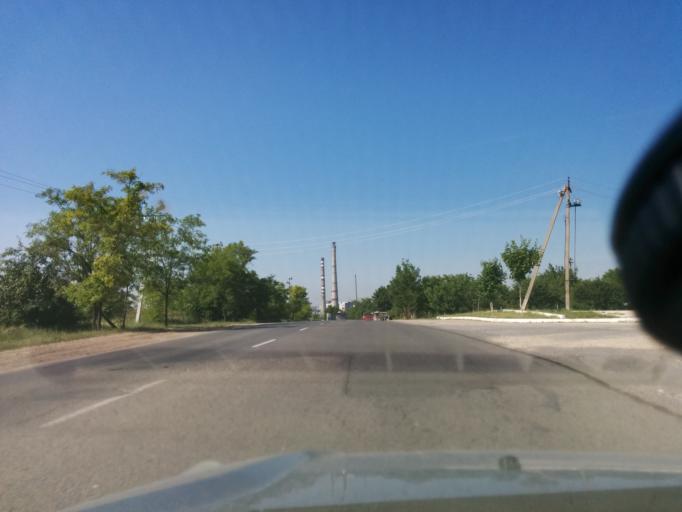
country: MD
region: Chisinau
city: Chisinau
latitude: 47.0428
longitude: 28.9063
